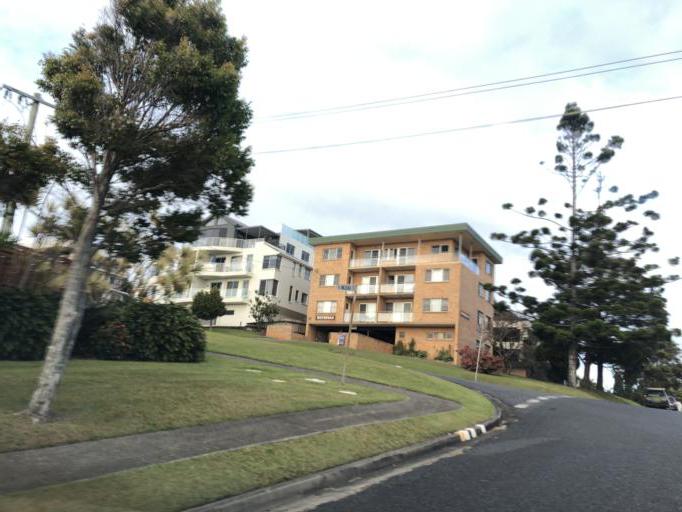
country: AU
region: New South Wales
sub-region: Coffs Harbour
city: Coffs Harbour
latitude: -30.3020
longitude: 153.1353
